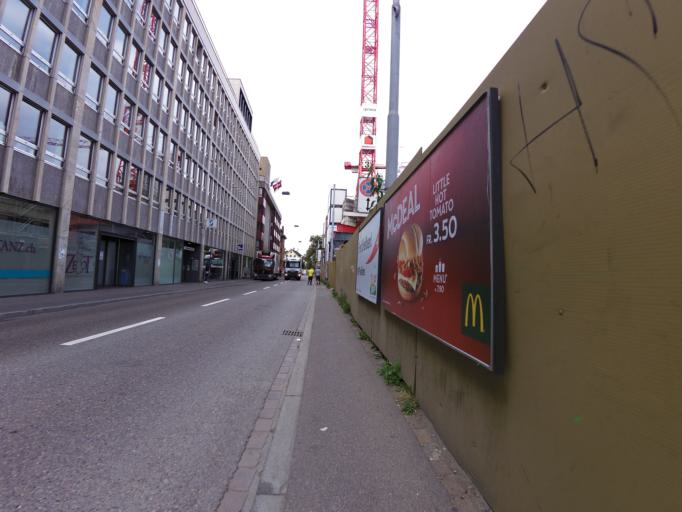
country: CH
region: Zurich
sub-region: Bezirk Zuerich
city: Zuerich (Kreis 4) / Langstrasse
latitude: 47.3796
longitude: 8.5294
